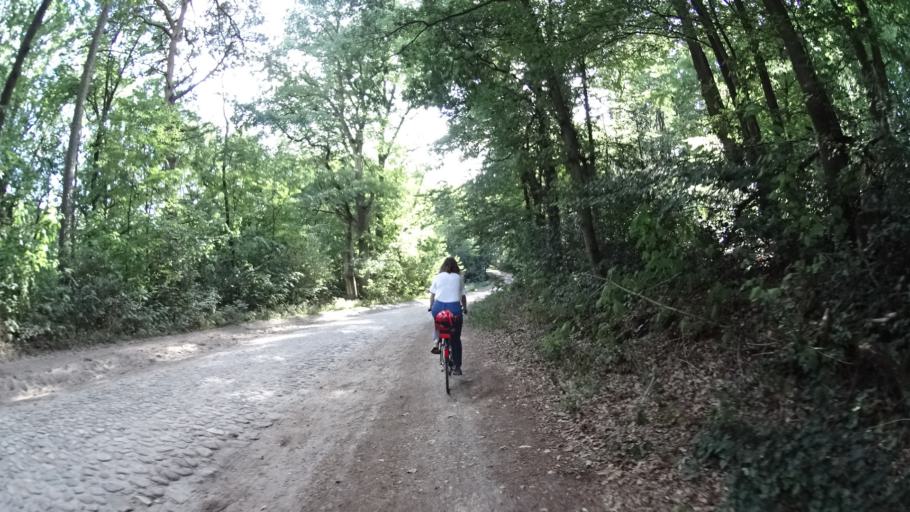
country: DE
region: Lower Saxony
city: Undeloh
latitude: 53.1497
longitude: 9.9125
